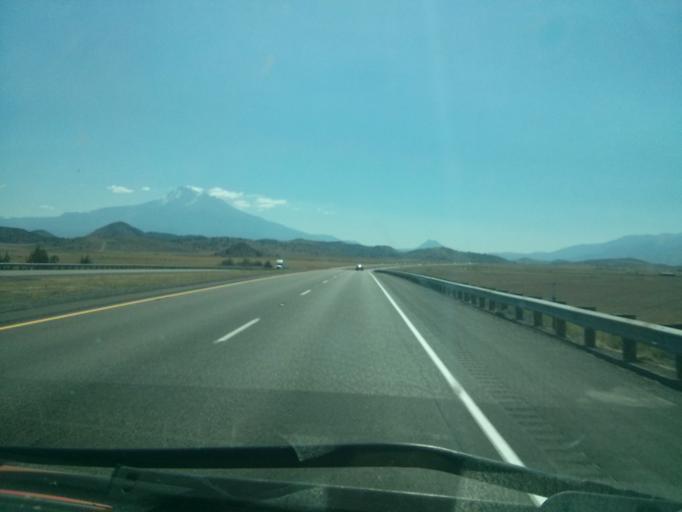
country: US
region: California
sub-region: Siskiyou County
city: Montague
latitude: 41.6270
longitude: -122.5216
